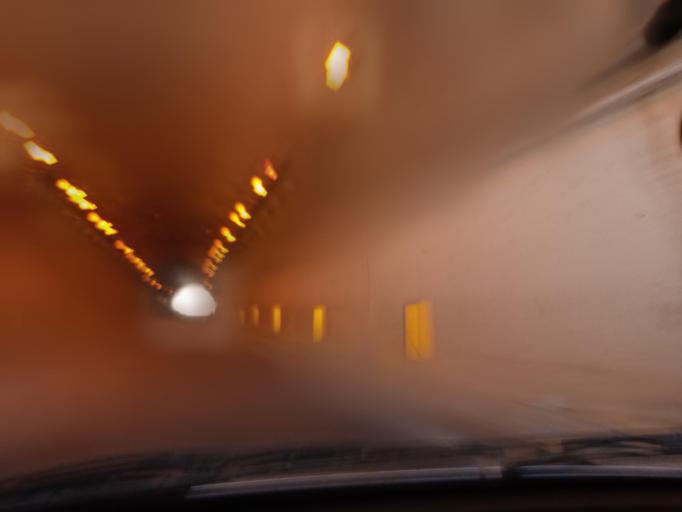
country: IT
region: Sicily
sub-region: Messina
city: Sant'Agata di Militello
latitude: 38.0750
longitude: 14.6600
